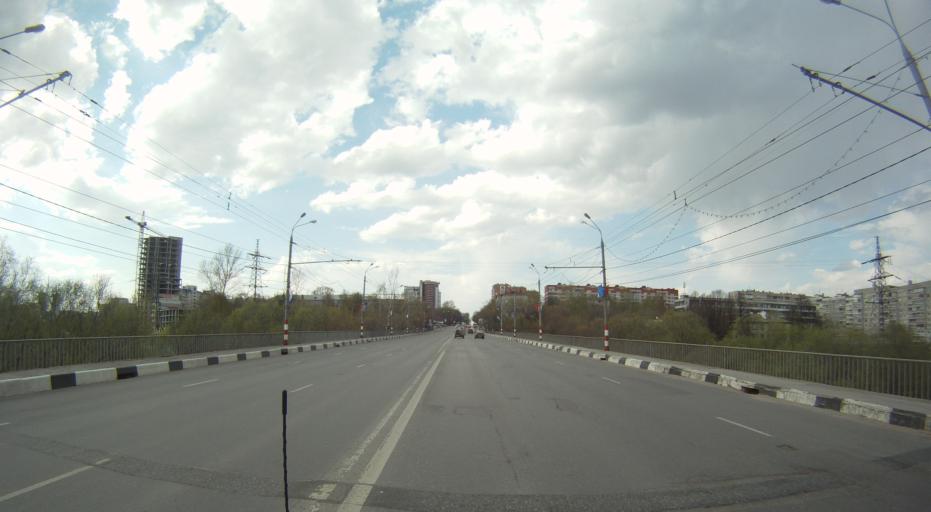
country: RU
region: Nizjnij Novgorod
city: Nizhniy Novgorod
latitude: 56.3057
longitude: 44.0260
